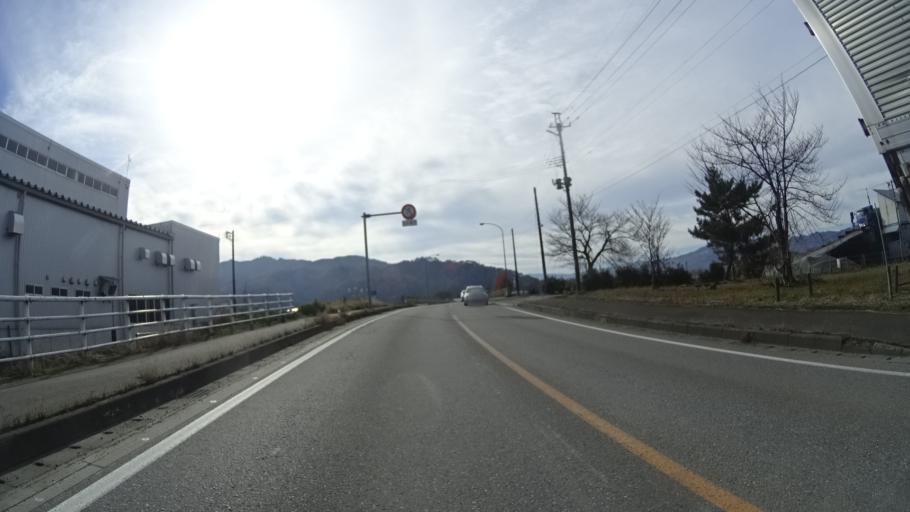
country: JP
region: Niigata
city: Muikamachi
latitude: 37.0878
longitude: 138.9116
